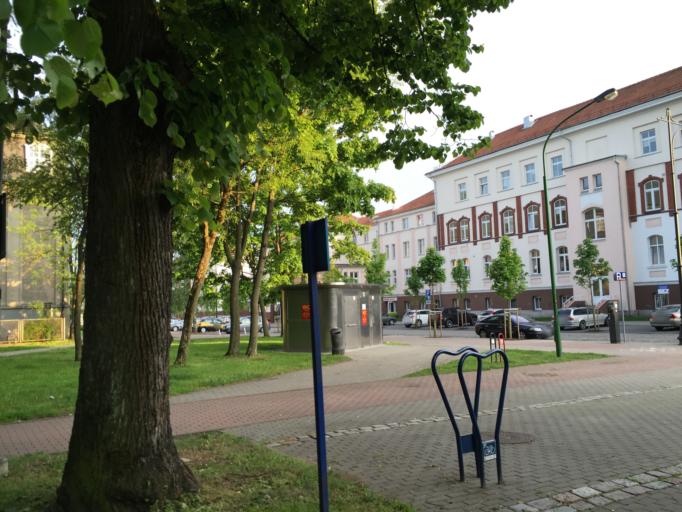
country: LT
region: Klaipedos apskritis
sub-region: Klaipeda
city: Klaipeda
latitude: 55.7155
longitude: 21.1361
